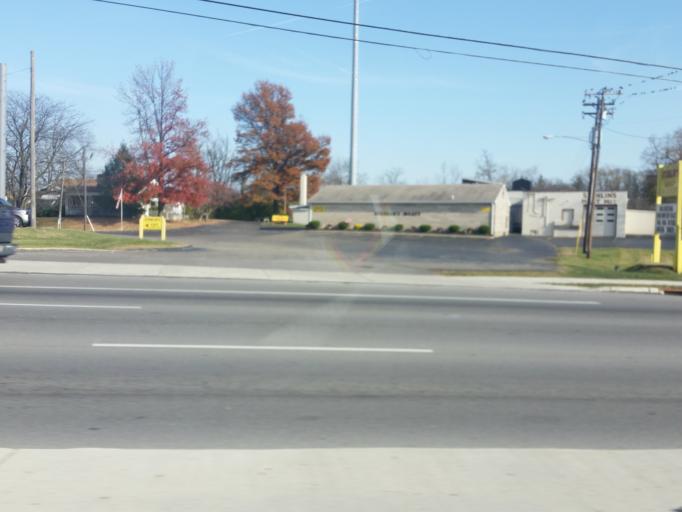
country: US
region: Ohio
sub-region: Hamilton County
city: Northgate
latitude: 39.2582
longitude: -84.6016
